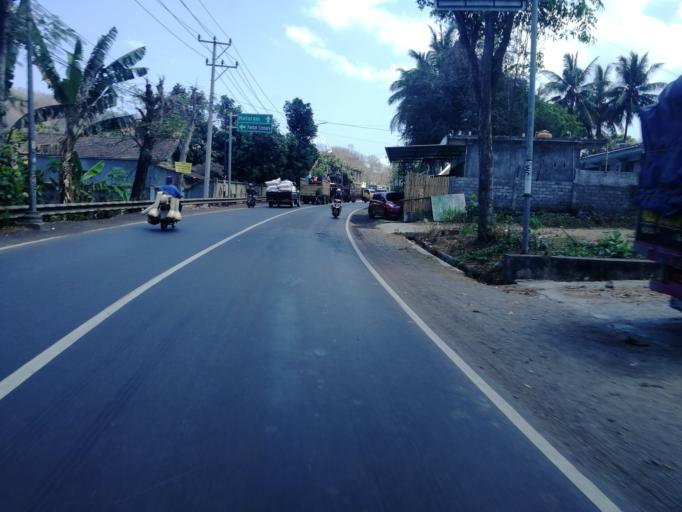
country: ID
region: West Nusa Tenggara
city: Jelateng Timur
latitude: -8.7199
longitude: 116.0737
